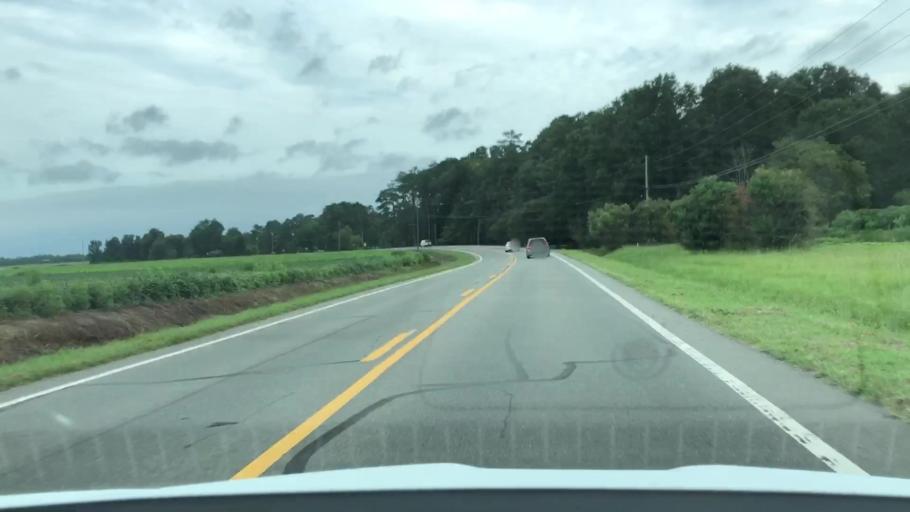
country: US
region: North Carolina
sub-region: Lenoir County
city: Kinston
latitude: 35.2025
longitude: -77.5617
